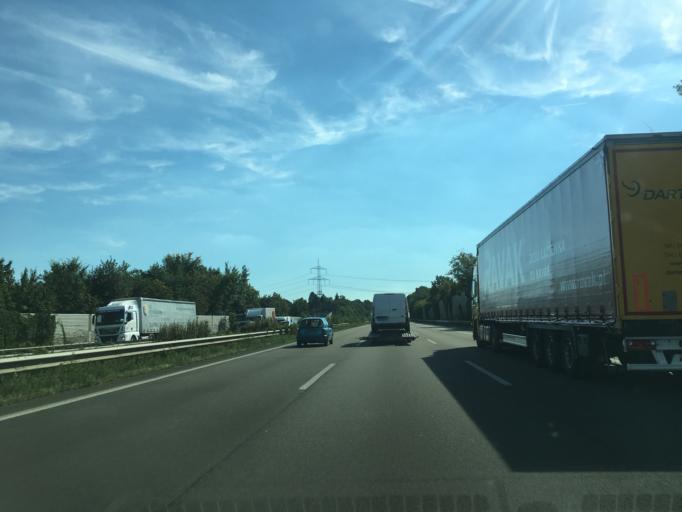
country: DE
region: North Rhine-Westphalia
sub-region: Regierungsbezirk Detmold
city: Leopoldshohe
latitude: 52.0497
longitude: 8.6551
